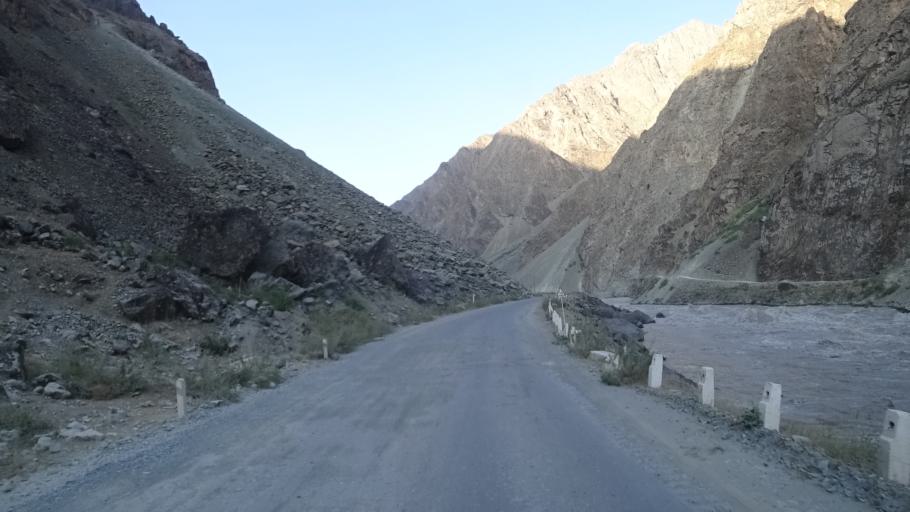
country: TJ
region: Gorno-Badakhshan
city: Qalaikhumb
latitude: 38.4247
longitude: 70.7482
